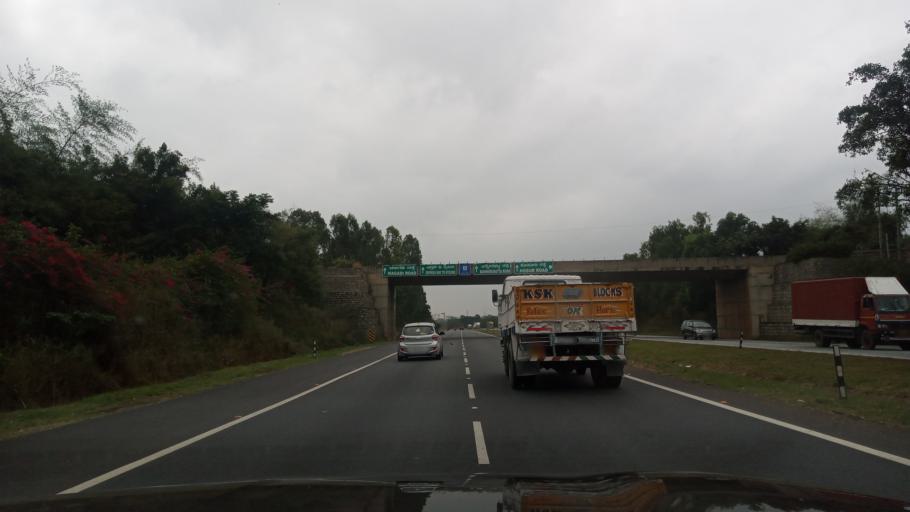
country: IN
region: Karnataka
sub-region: Bangalore Rural
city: Nelamangala
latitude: 13.0268
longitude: 77.4755
